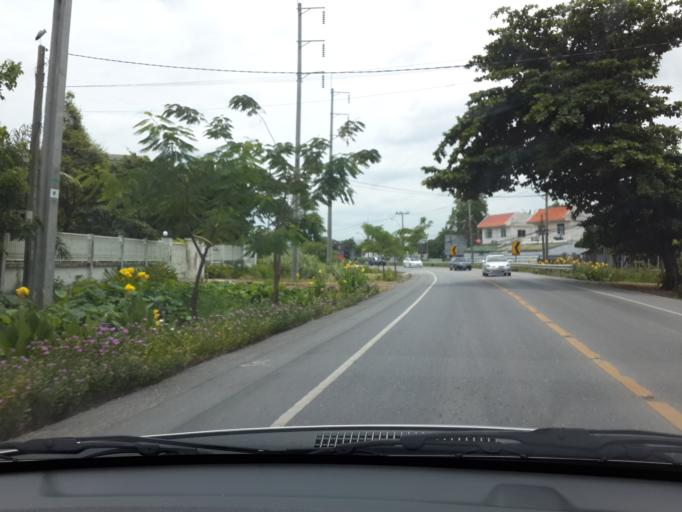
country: TH
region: Bangkok
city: Khlong Sam Wa
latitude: 13.8247
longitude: 100.7504
